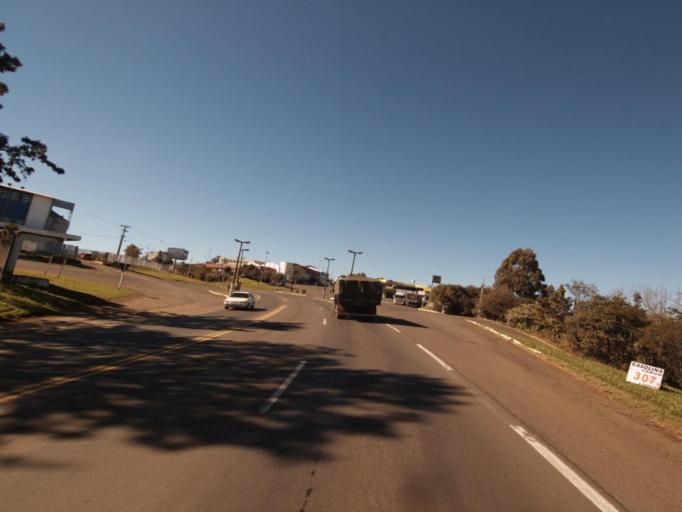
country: BR
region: Santa Catarina
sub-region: Chapeco
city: Chapeco
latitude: -26.9869
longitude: -52.6059
